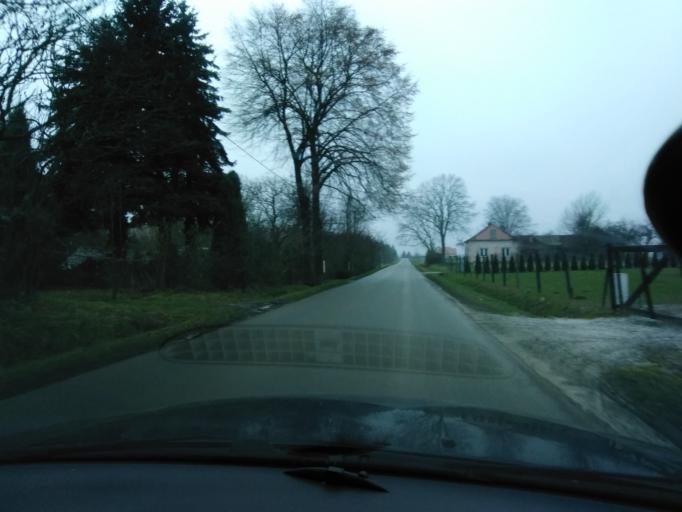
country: PL
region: Subcarpathian Voivodeship
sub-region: Powiat przeworski
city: Zurawiczki
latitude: 50.0019
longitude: 22.4940
